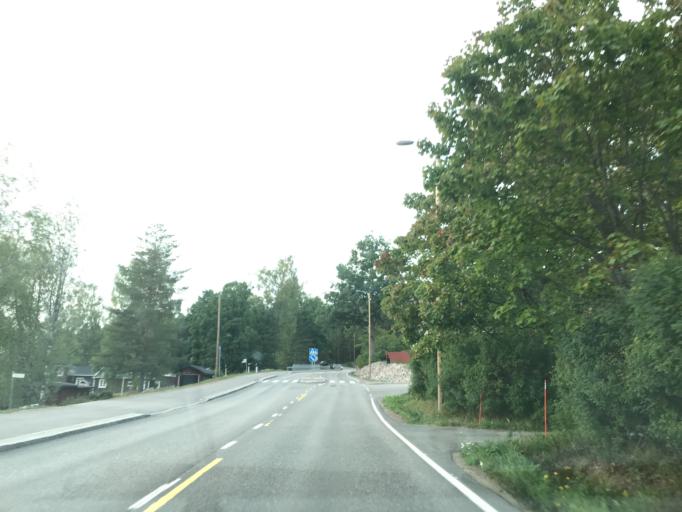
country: FI
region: Uusimaa
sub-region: Helsinki
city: Kirkkonummi
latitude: 60.2524
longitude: 24.4506
